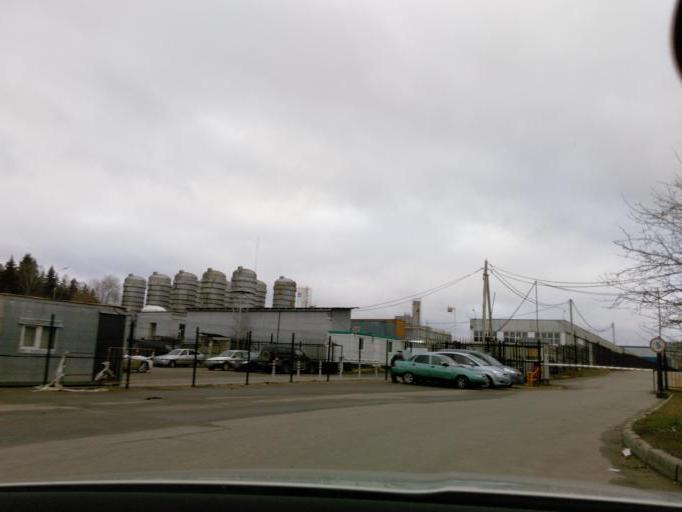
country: RU
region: Moskovskaya
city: Rzhavki
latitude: 55.9826
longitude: 37.2226
